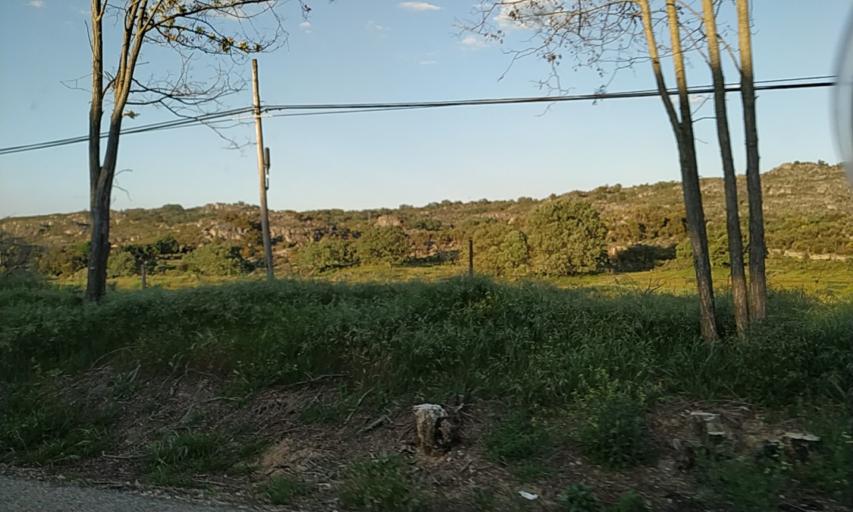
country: PT
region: Portalegre
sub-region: Portalegre
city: Sao Juliao
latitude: 39.3560
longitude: -7.2750
